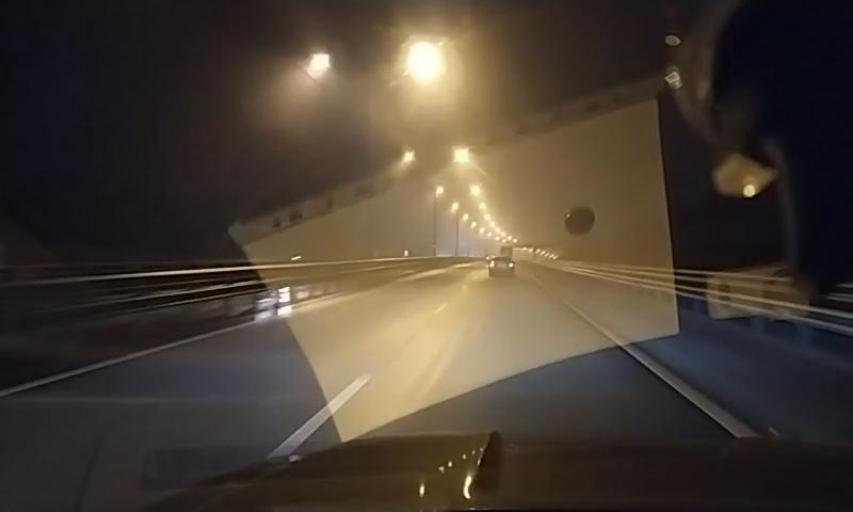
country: RU
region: Leningrad
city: Bugry
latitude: 60.1182
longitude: 30.3861
